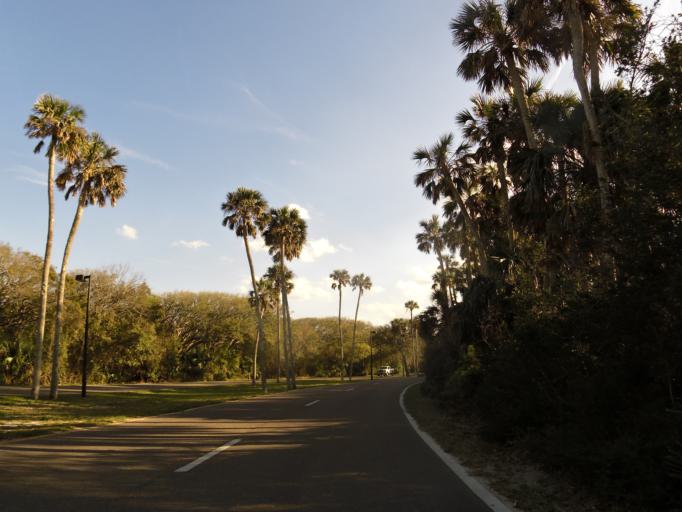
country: US
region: Florida
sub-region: Duval County
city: Atlantic Beach
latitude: 30.3654
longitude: -81.4003
